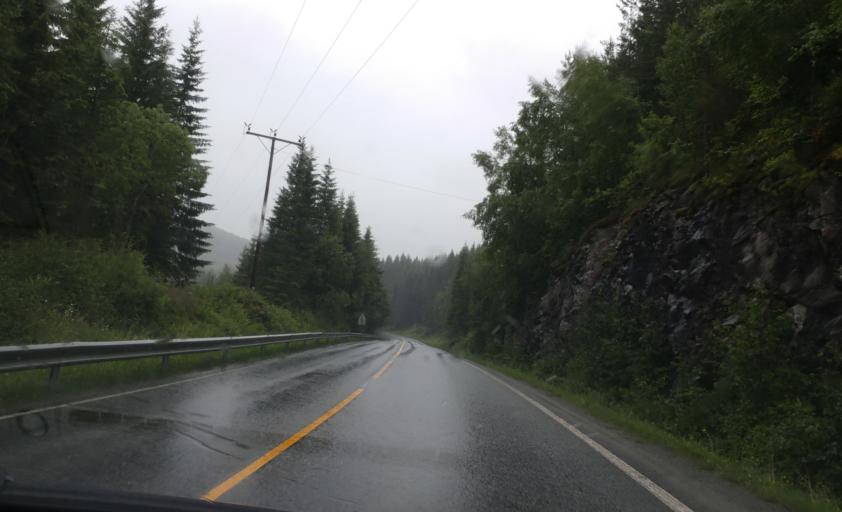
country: NO
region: Nord-Trondelag
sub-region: Stjordal
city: Stjordalshalsen
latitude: 63.3979
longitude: 10.9516
